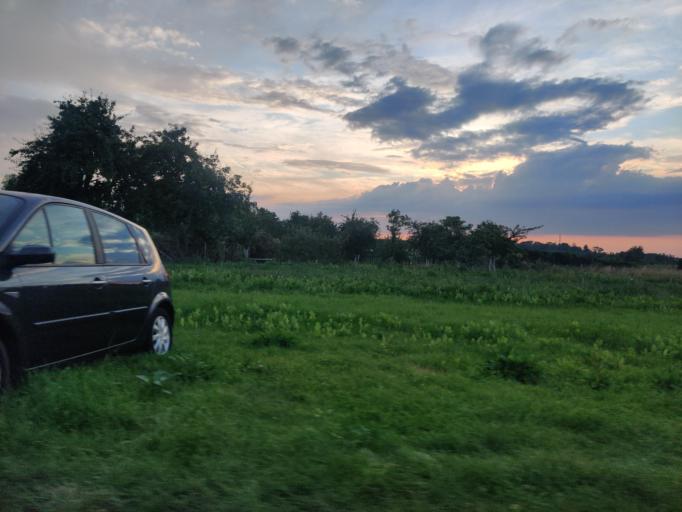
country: PL
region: Greater Poland Voivodeship
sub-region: Konin
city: Konin
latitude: 52.1928
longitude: 18.3138
